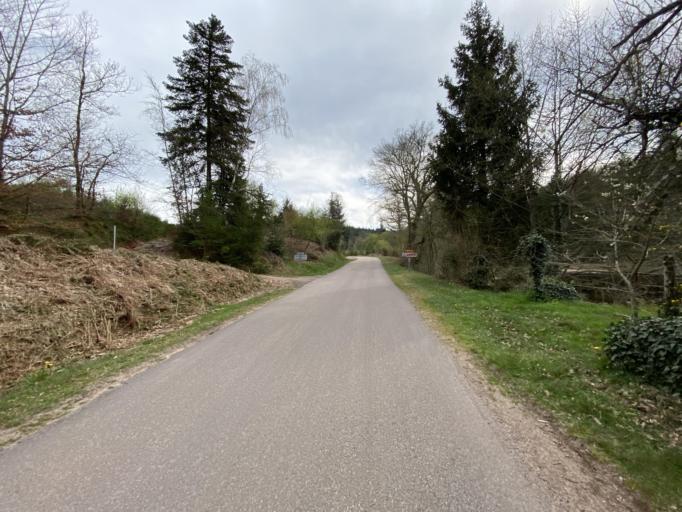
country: FR
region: Bourgogne
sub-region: Departement de la Cote-d'Or
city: Saulieu
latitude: 47.3170
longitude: 4.0942
